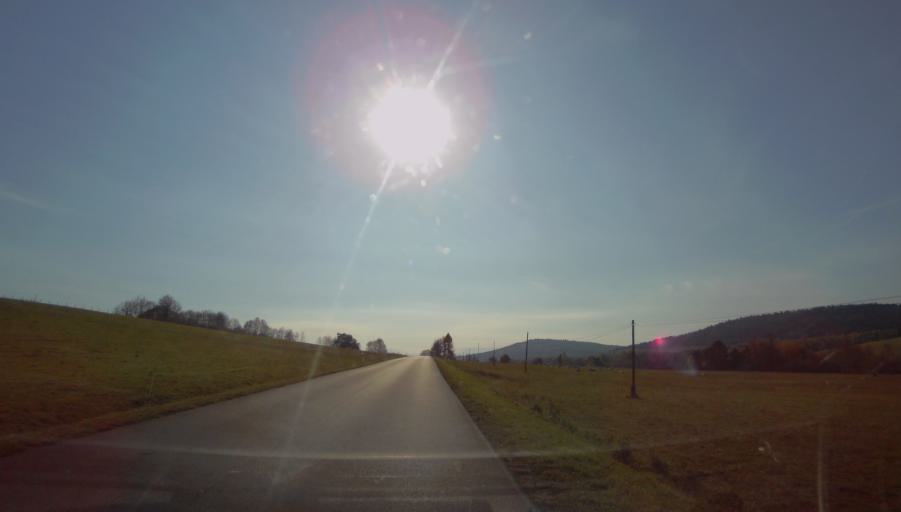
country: PL
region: Subcarpathian Voivodeship
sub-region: Powiat sanocki
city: Komancza
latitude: 49.2995
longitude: 22.0573
